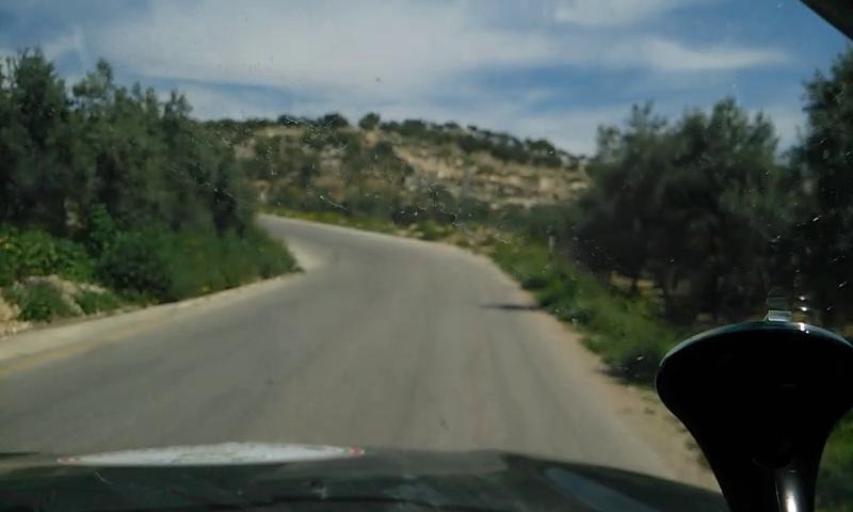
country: PS
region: West Bank
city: Kharbatha al Misbah
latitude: 31.8808
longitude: 35.0787
